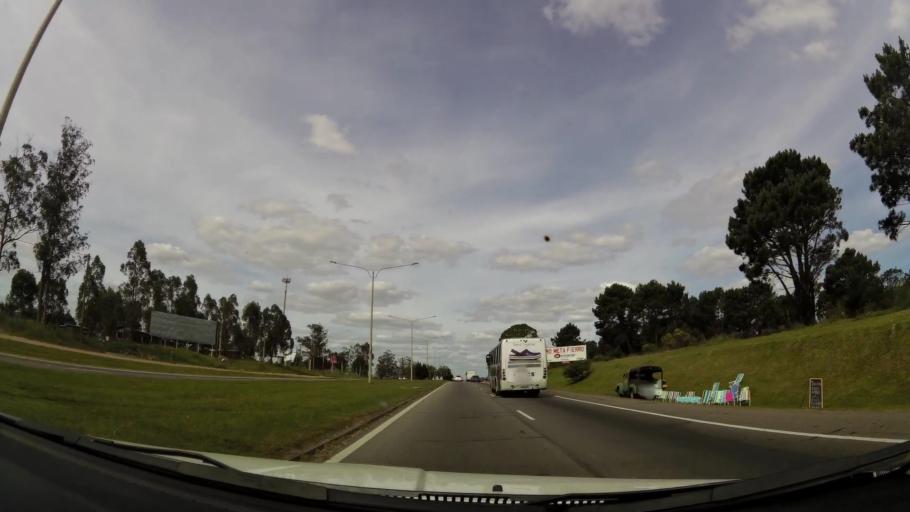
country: UY
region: Canelones
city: Empalme Olmos
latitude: -34.7824
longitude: -55.8809
